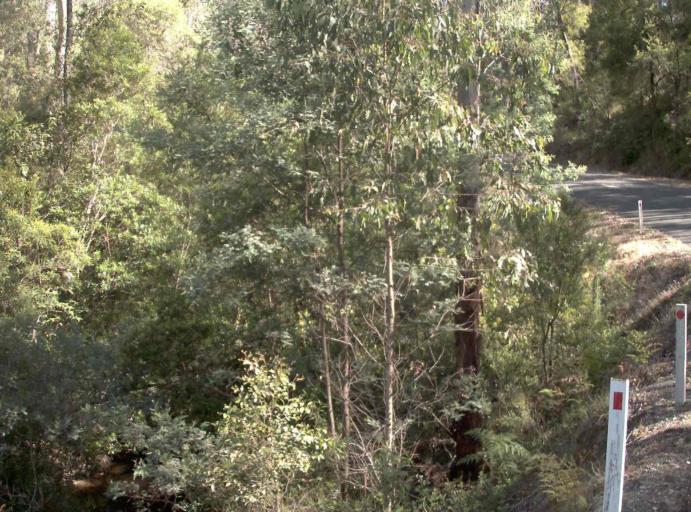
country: AU
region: Victoria
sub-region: East Gippsland
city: Lakes Entrance
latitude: -37.4747
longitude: 148.5578
